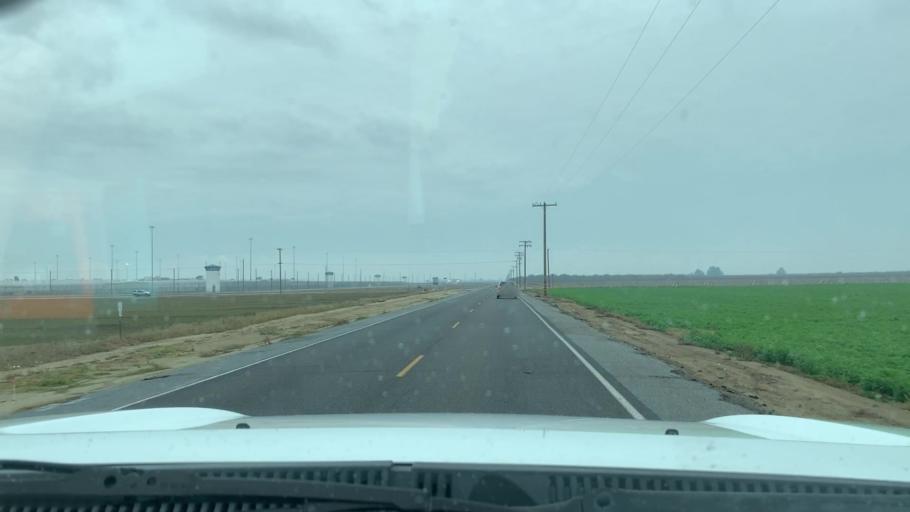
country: US
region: California
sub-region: Kern County
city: Delano
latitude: 35.7612
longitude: -119.3320
